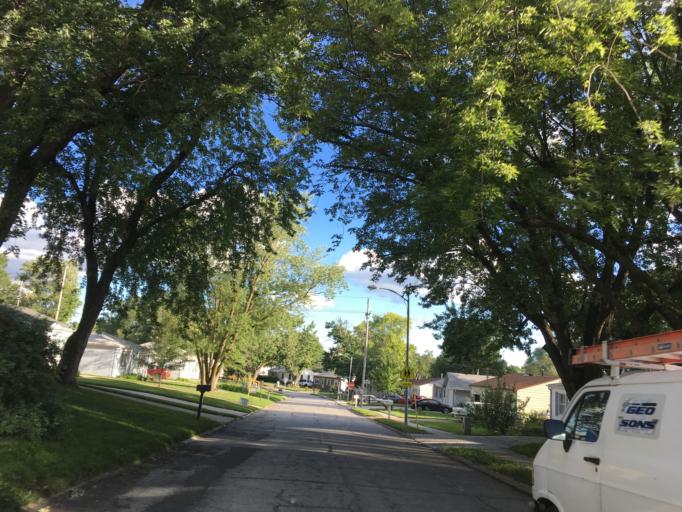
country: US
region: Nebraska
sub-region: Sarpy County
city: La Vista
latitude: 41.1842
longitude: -95.9732
